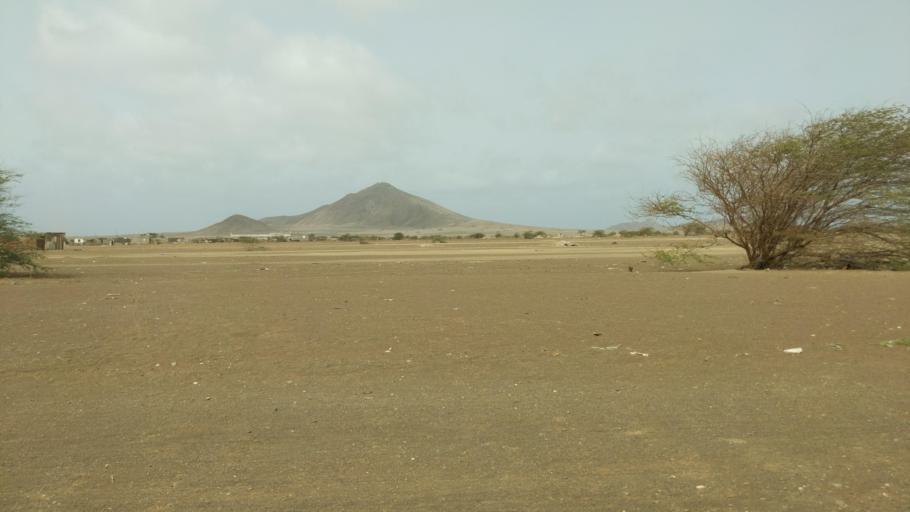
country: CV
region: Sal
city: Espargos
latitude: 16.7703
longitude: -22.9461
